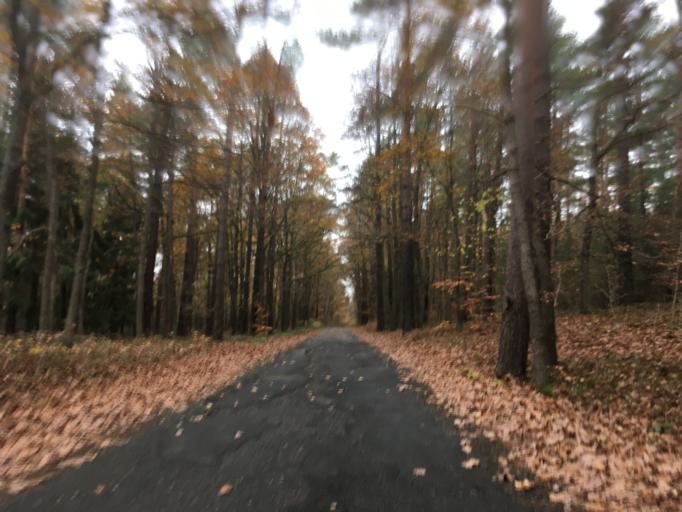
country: DE
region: Brandenburg
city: Mixdorf
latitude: 52.1750
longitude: 14.4366
